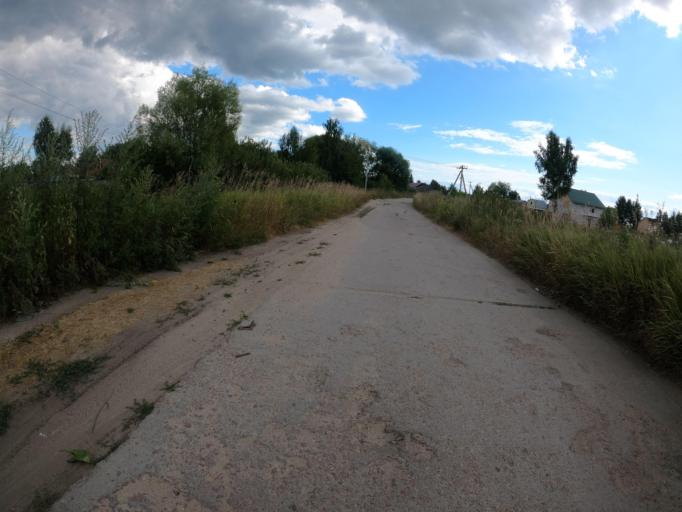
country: RU
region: Moskovskaya
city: Konobeyevo
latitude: 55.3981
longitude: 38.6755
